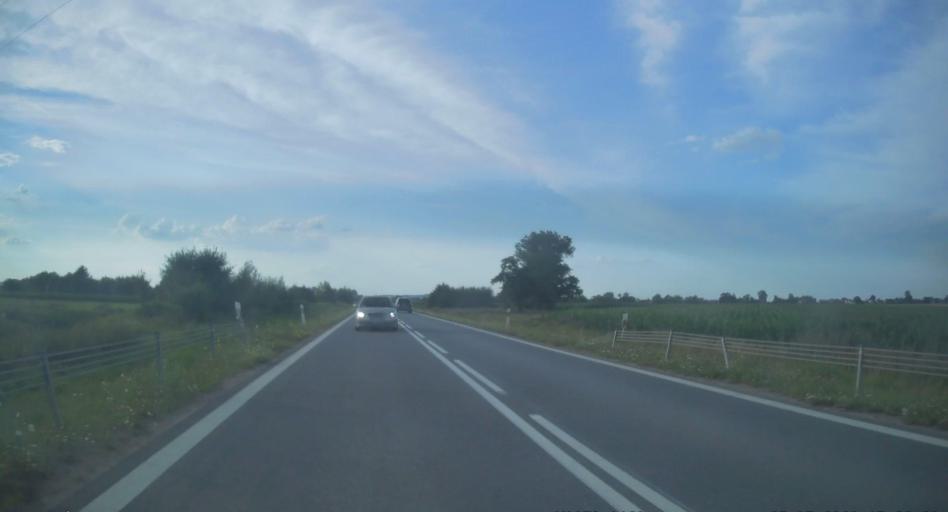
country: PL
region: Lesser Poland Voivodeship
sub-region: Powiat brzeski
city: Szczurowa
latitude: 50.1120
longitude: 20.6180
